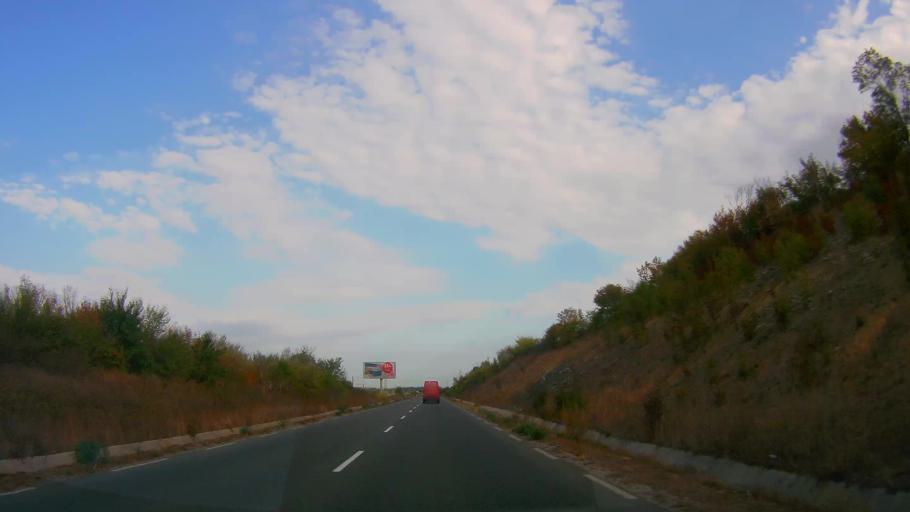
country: BG
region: Burgas
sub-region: Obshtina Sozopol
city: Sozopol
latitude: 42.3882
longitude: 27.6785
